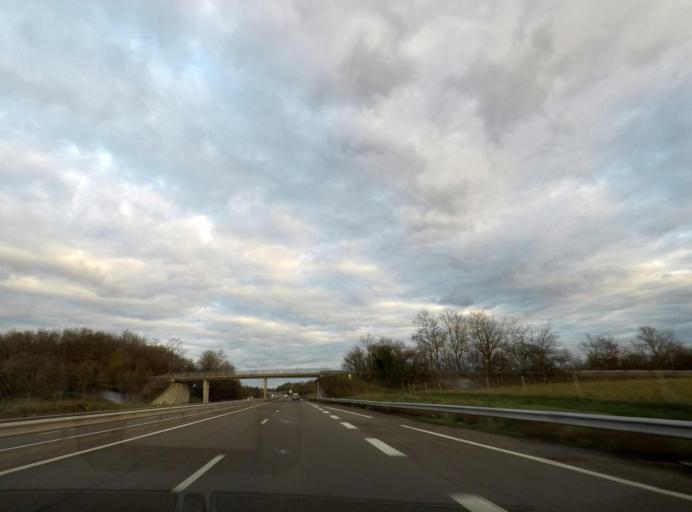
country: FR
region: Rhone-Alpes
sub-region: Departement de l'Ain
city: Mezeriat
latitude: 46.2712
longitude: 5.0215
